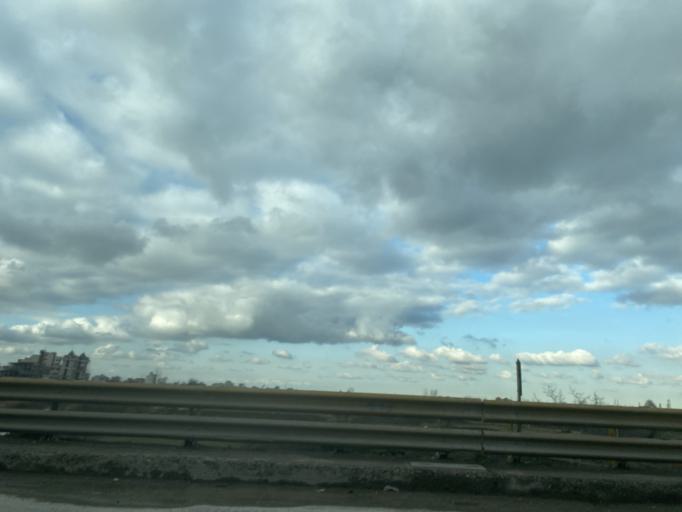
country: IR
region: Mazandaran
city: Amol
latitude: 36.4333
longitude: 52.3521
